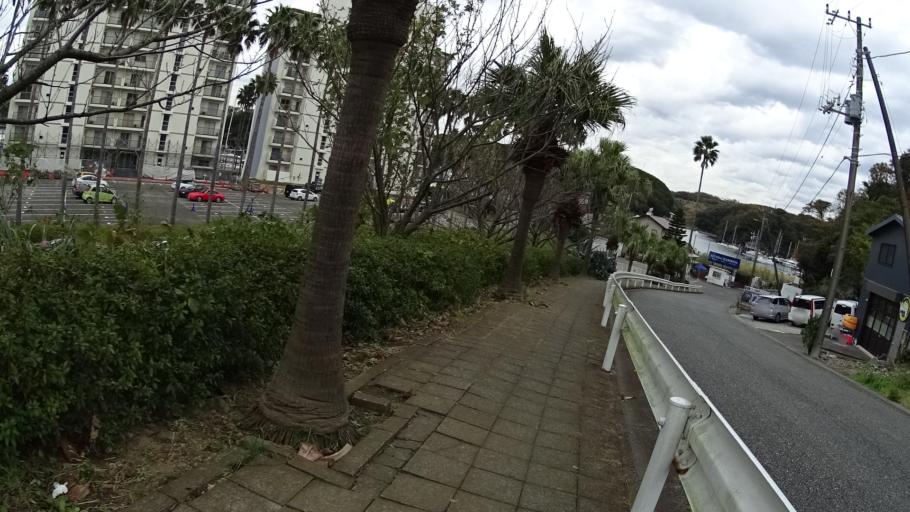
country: JP
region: Kanagawa
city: Miura
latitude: 35.1619
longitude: 139.6216
